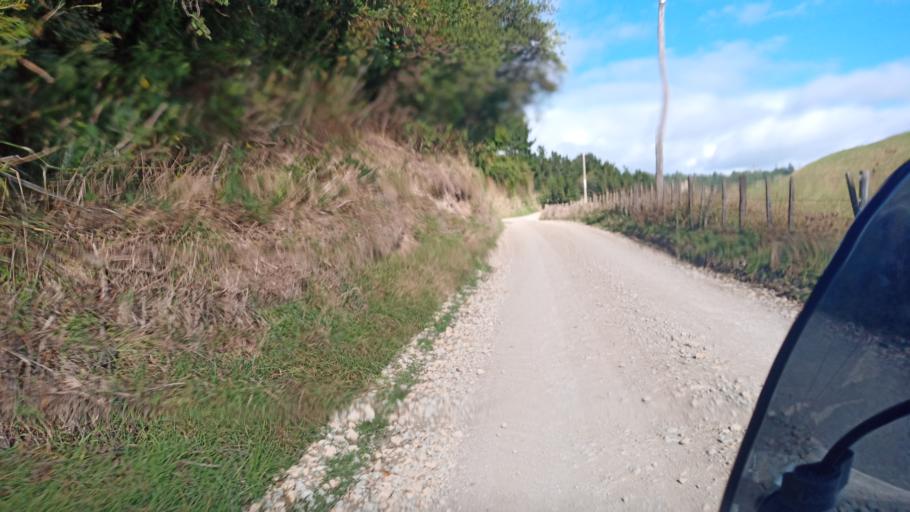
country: NZ
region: Gisborne
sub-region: Gisborne District
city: Gisborne
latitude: -38.5405
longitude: 177.5112
